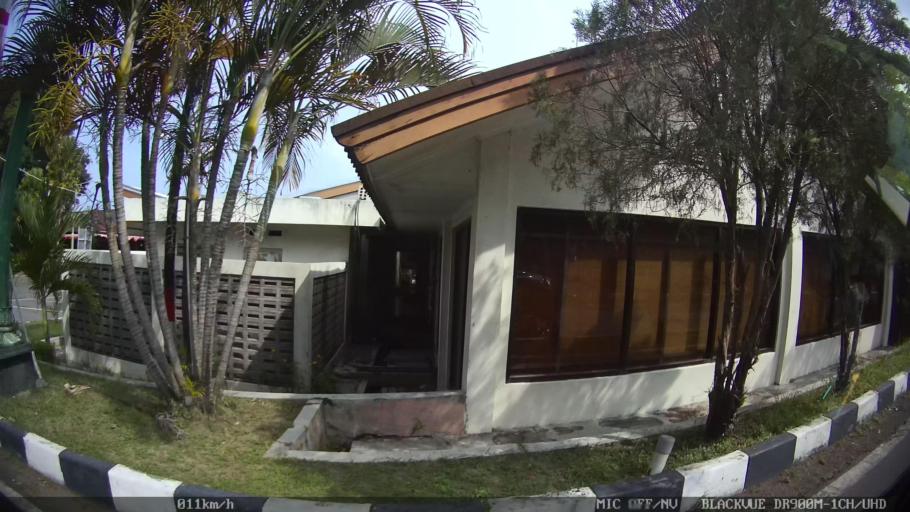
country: ID
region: Daerah Istimewa Yogyakarta
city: Depok
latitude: -7.7853
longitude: 110.4373
